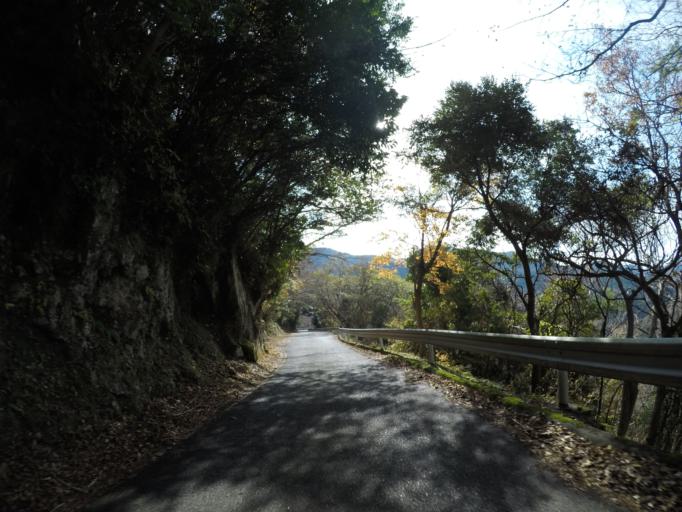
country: JP
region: Shizuoka
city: Heda
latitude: 34.8325
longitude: 138.8524
